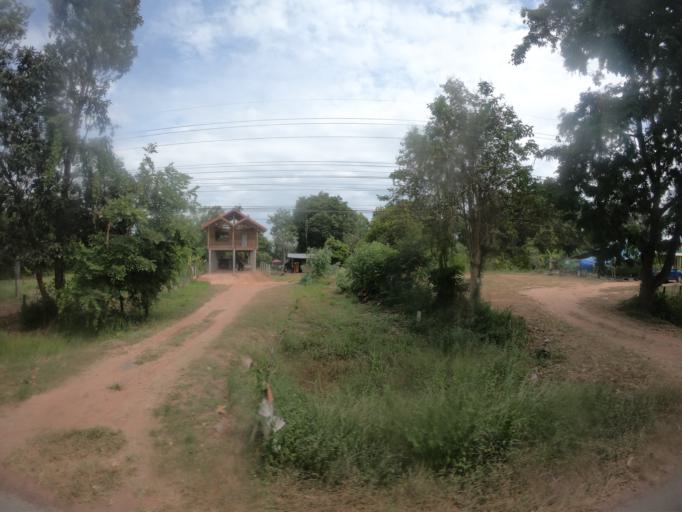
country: TH
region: Maha Sarakham
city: Chiang Yuen
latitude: 16.3539
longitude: 103.1168
